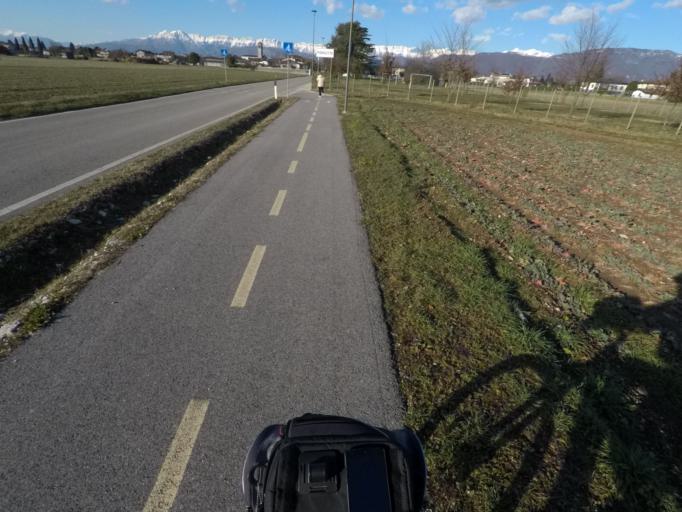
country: IT
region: Friuli Venezia Giulia
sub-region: Provincia di Udine
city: Povoletto
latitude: 46.1134
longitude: 13.2997
